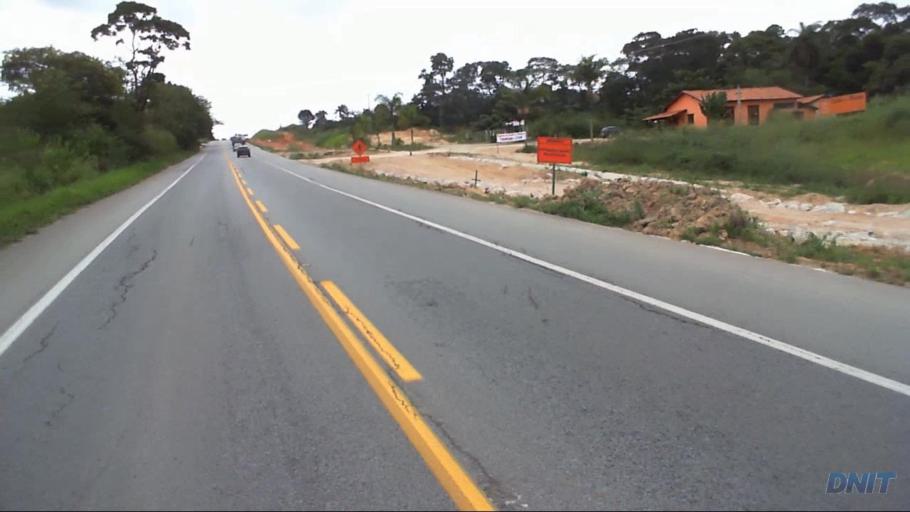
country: BR
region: Minas Gerais
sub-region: Barao De Cocais
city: Barao de Cocais
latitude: -19.7492
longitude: -43.4872
